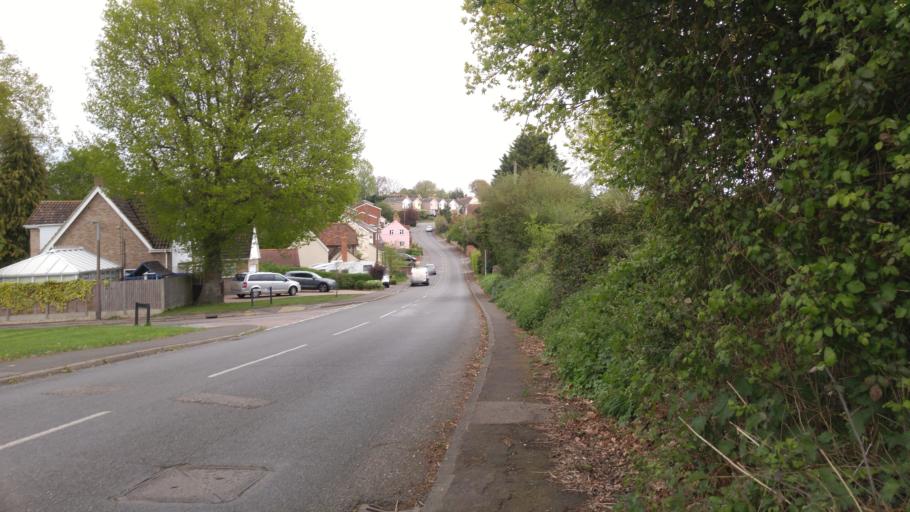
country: GB
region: England
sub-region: Essex
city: Earls Colne
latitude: 51.9410
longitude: 0.6841
